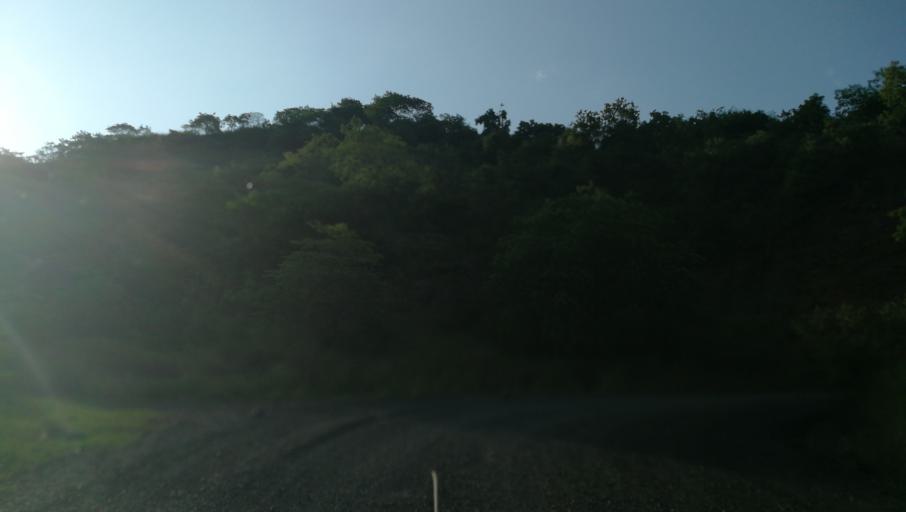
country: ET
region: Southern Nations, Nationalities, and People's Region
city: Areka
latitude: 6.8372
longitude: 37.2783
